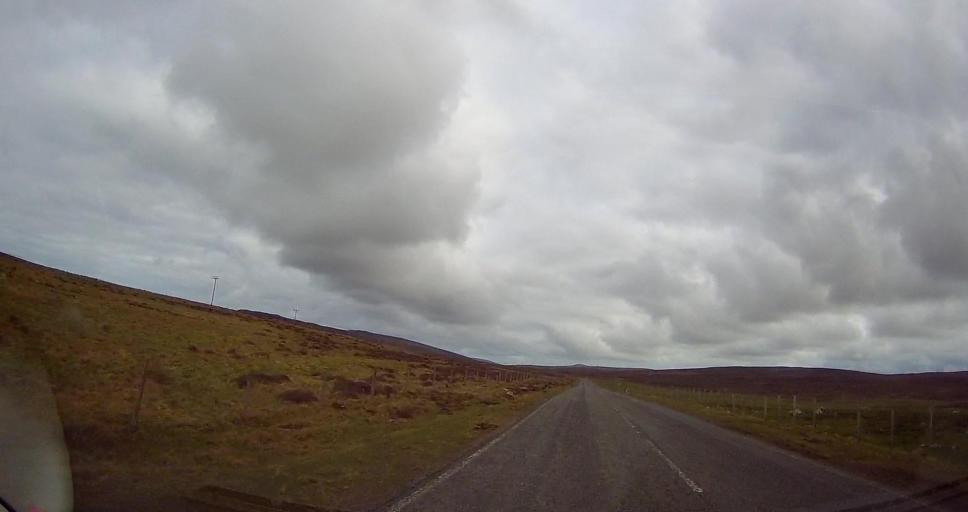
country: GB
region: Scotland
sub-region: Shetland Islands
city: Shetland
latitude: 60.6965
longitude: -0.9227
